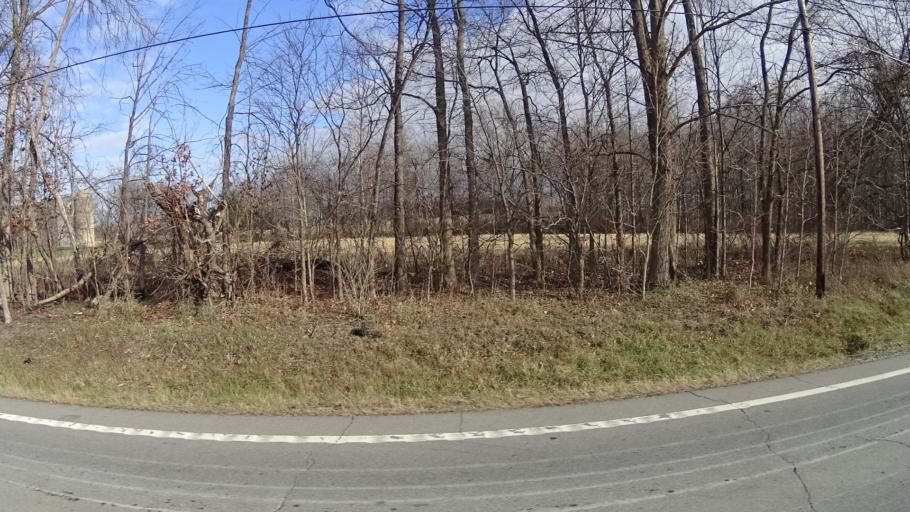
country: US
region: Ohio
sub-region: Lorain County
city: Wellington
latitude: 41.1359
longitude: -82.3074
